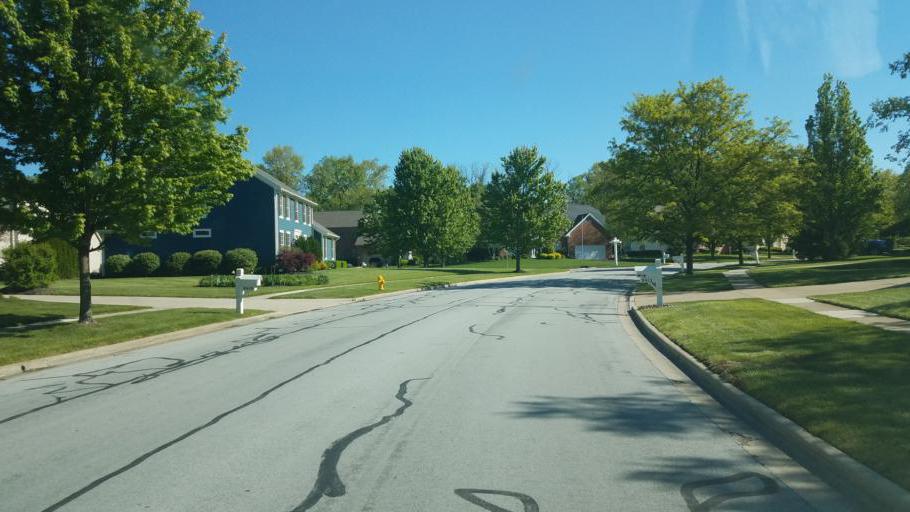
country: US
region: Ohio
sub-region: Franklin County
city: Westerville
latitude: 40.1549
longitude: -82.9316
